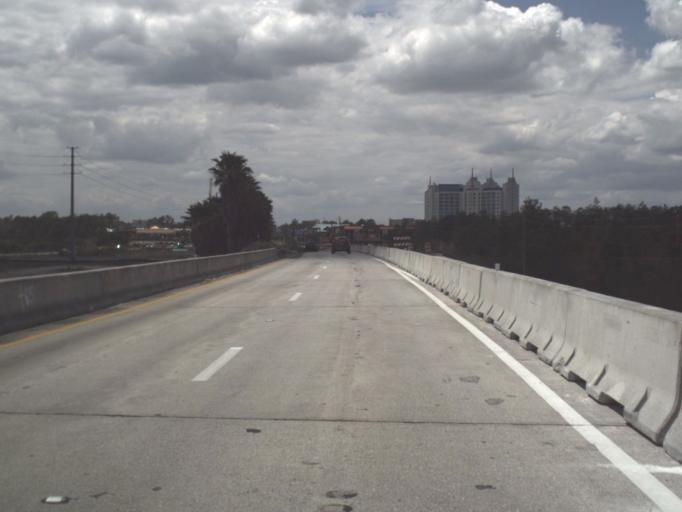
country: US
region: Florida
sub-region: Orange County
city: Tangelo Park
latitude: 28.4513
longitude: -81.4587
